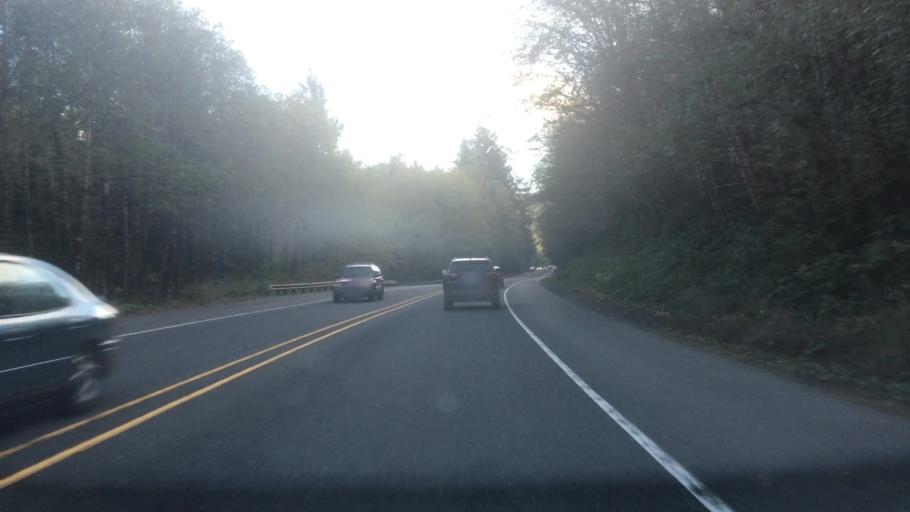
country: US
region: Oregon
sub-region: Clatsop County
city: Cannon Beach
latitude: 45.9306
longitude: -123.9279
